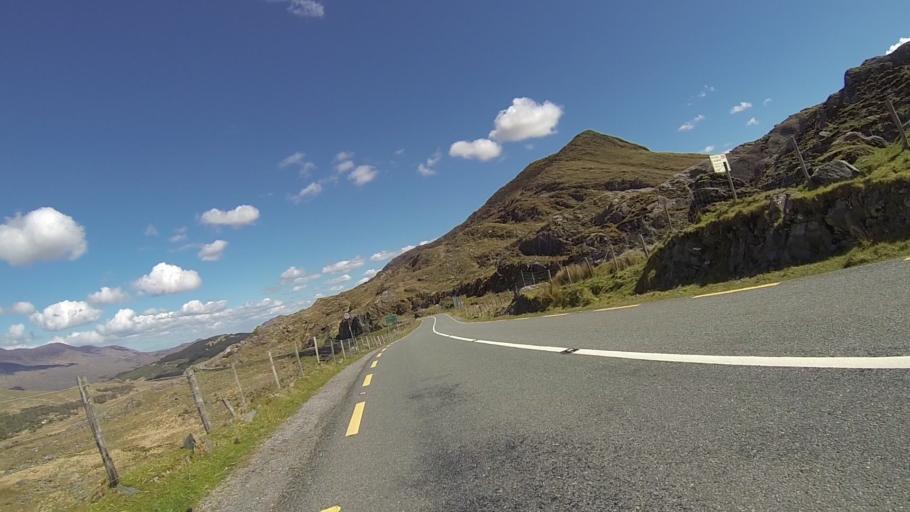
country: IE
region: Munster
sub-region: Ciarrai
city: Kenmare
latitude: 51.9387
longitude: -9.6572
